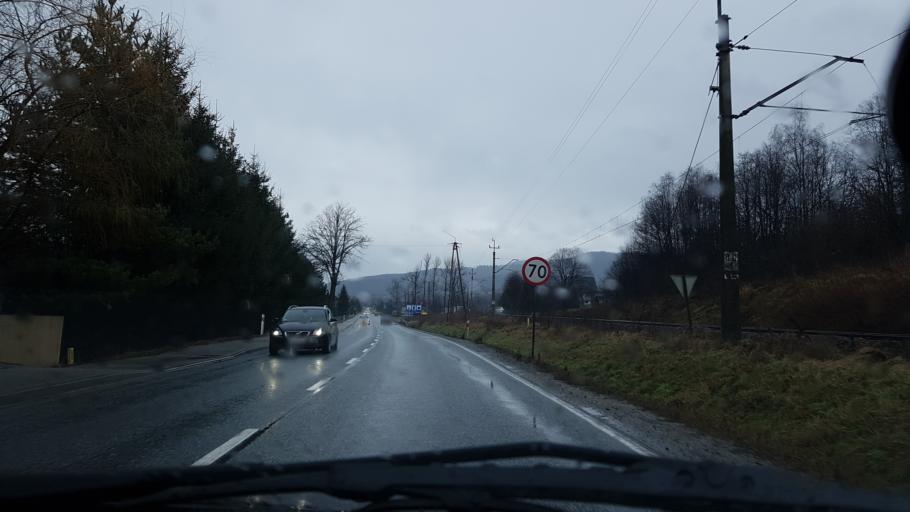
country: PL
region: Lesser Poland Voivodeship
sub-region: Powiat suski
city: Juszczyn
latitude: 49.7065
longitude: 19.6927
